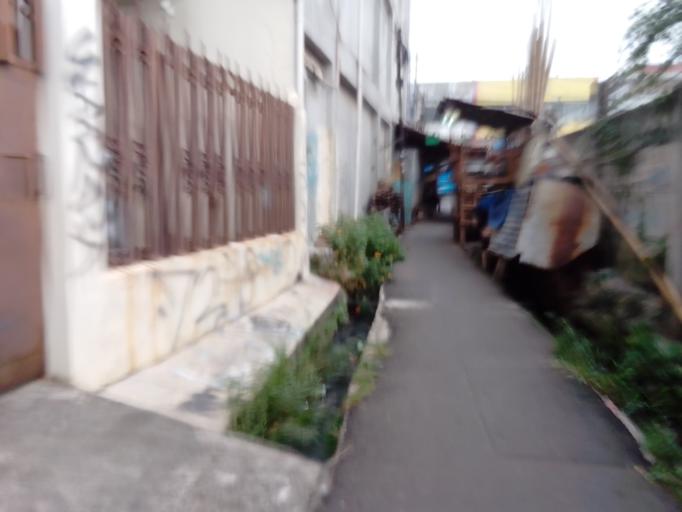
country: ID
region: Jakarta Raya
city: Jakarta
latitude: -6.1656
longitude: 106.8050
